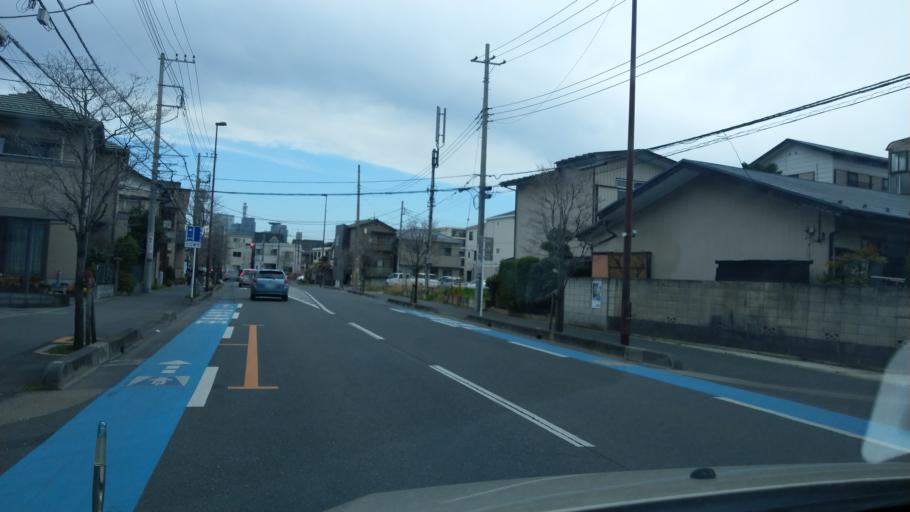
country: JP
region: Saitama
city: Yono
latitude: 35.8731
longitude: 139.6336
